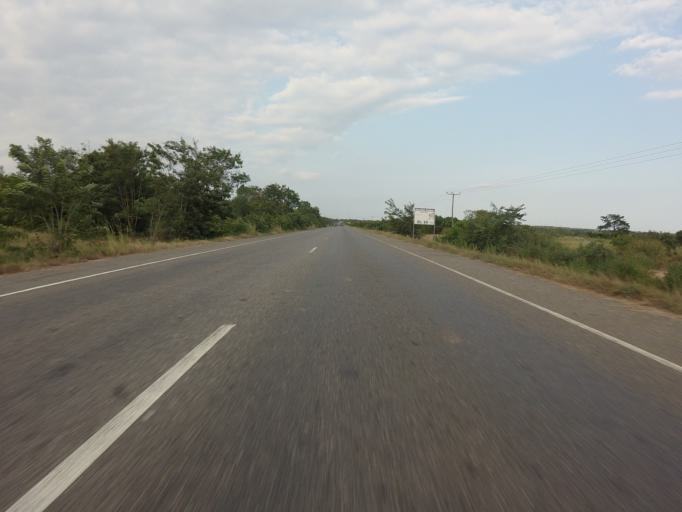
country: GH
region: Volta
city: Anloga
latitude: 6.0883
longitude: 0.5149
